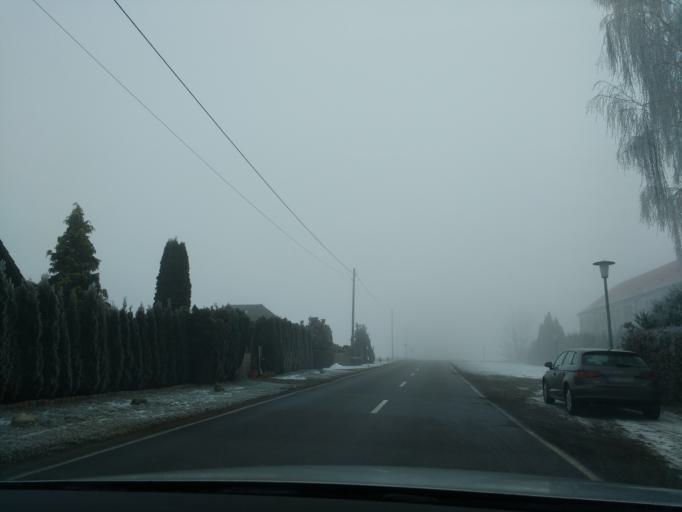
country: DE
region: Saxony-Anhalt
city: Oppin
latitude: 51.5502
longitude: 12.0381
